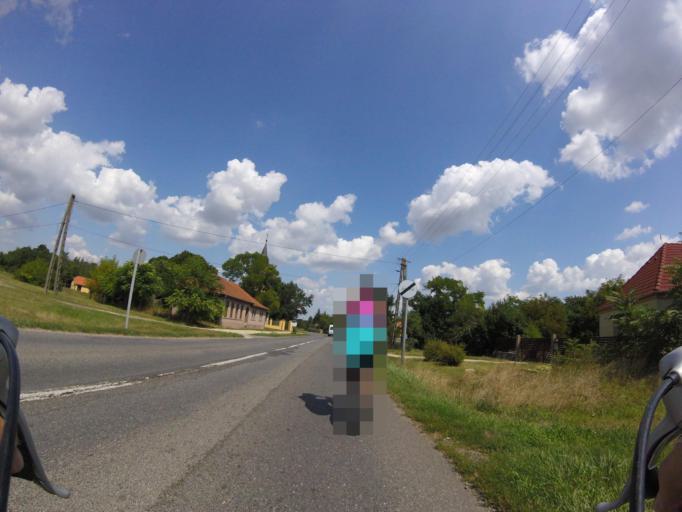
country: HU
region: Gyor-Moson-Sopron
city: Tet
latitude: 47.4889
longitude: 17.4954
